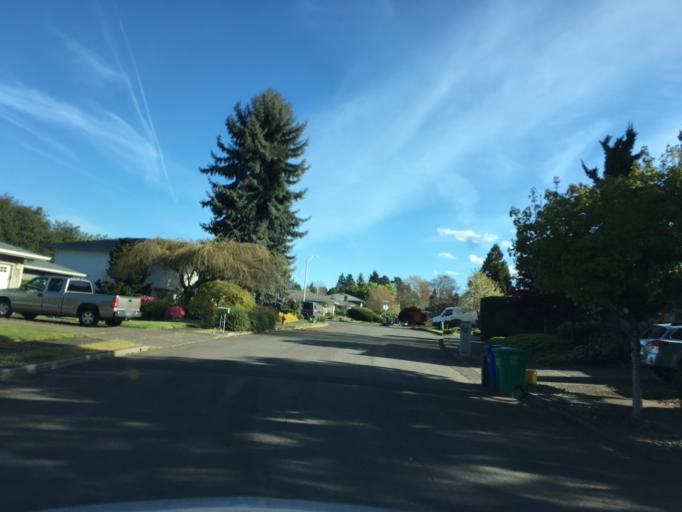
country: US
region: Oregon
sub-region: Multnomah County
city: Fairview
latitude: 45.5520
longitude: -122.5168
